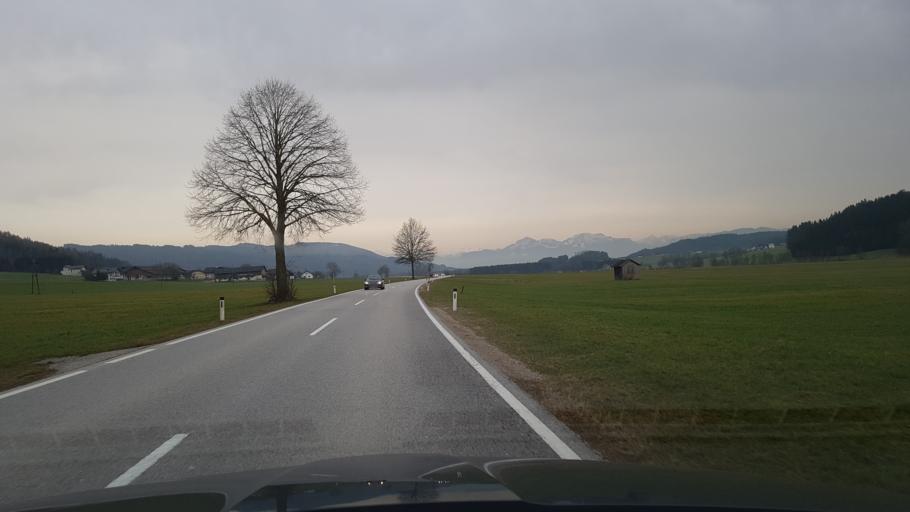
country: AT
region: Salzburg
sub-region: Politischer Bezirk Salzburg-Umgebung
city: Nussdorf am Haunsberg
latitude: 47.9805
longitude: 13.0118
